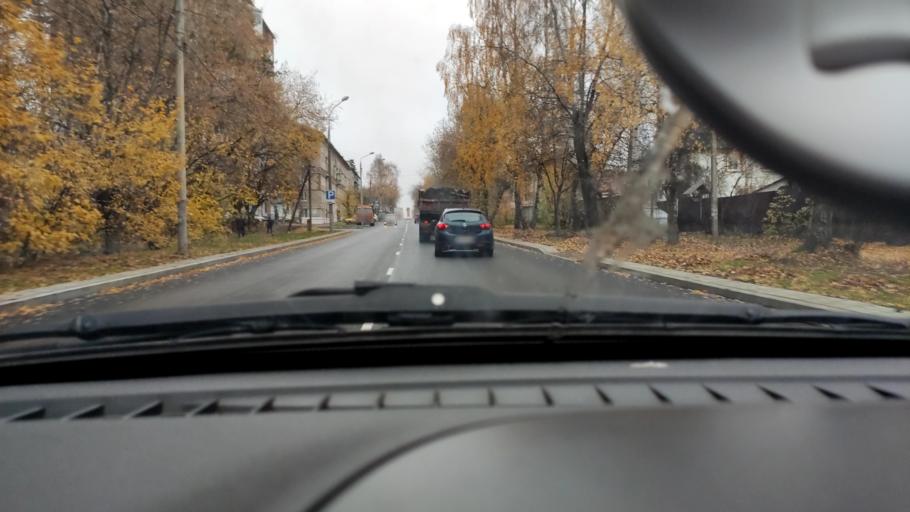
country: RU
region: Perm
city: Kondratovo
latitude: 58.0220
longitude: 56.0125
